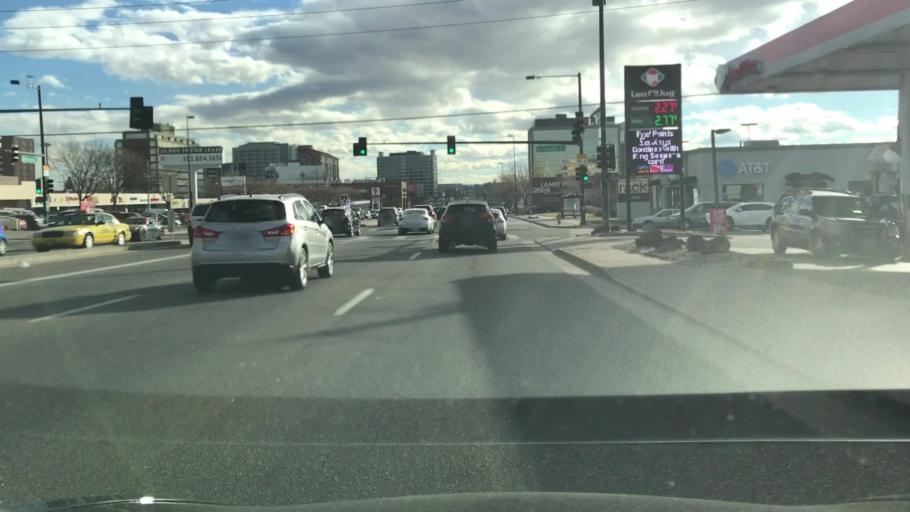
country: US
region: Colorado
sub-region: Arapahoe County
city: Glendale
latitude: 39.6898
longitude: -104.9408
